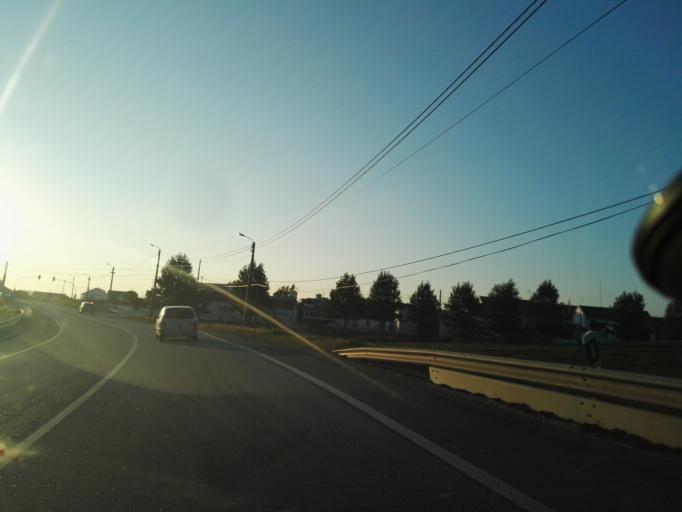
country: PT
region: Evora
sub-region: Vendas Novas
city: Vendas Novas
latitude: 38.6514
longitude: -8.3492
